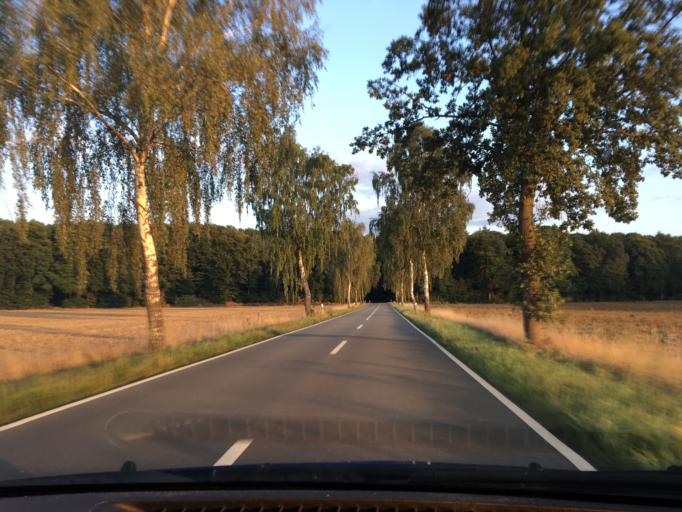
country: DE
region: Lower Saxony
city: Tosterglope
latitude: 53.2330
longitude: 10.7972
